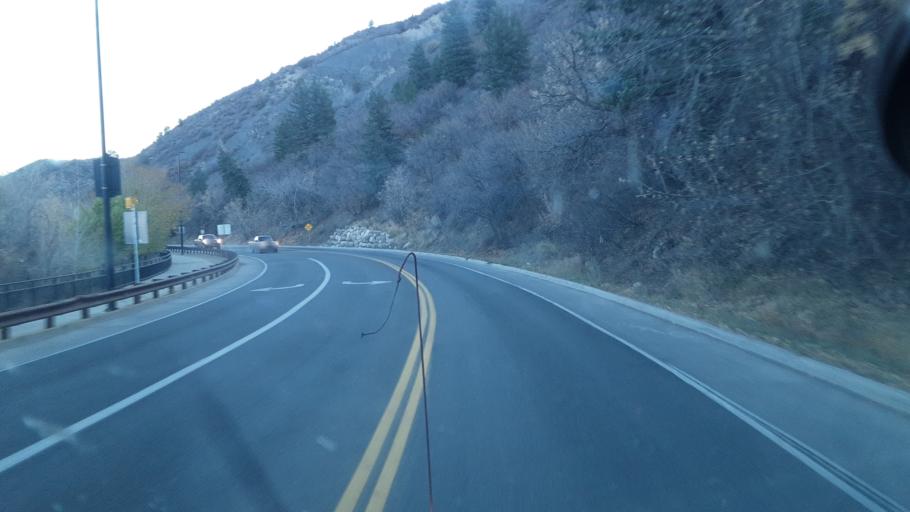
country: US
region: Colorado
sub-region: La Plata County
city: Durango
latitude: 37.2796
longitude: -107.8749
